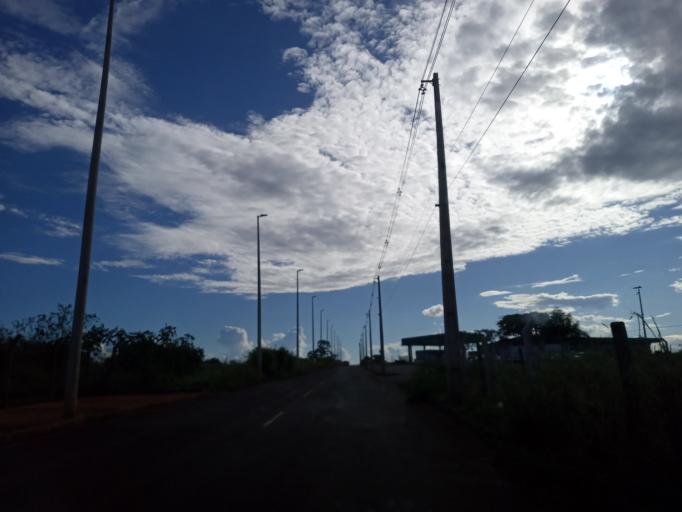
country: BR
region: Minas Gerais
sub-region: Ituiutaba
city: Ituiutaba
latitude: -18.9607
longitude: -49.4940
